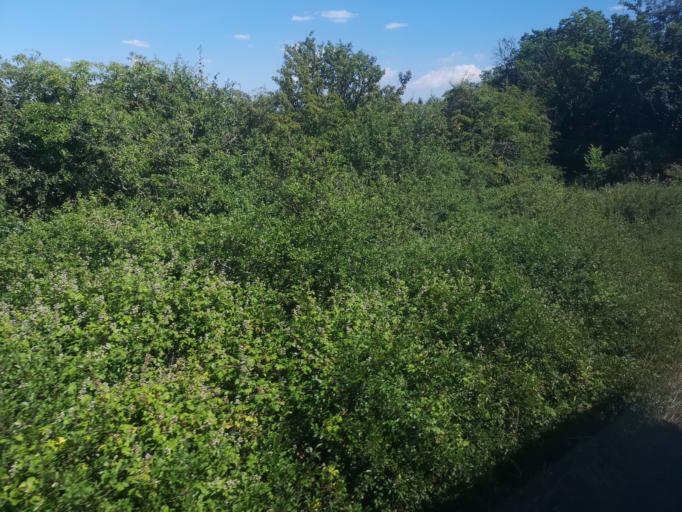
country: GB
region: England
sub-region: Isle of Wight
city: Yarmouth
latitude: 50.7025
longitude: -1.4851
